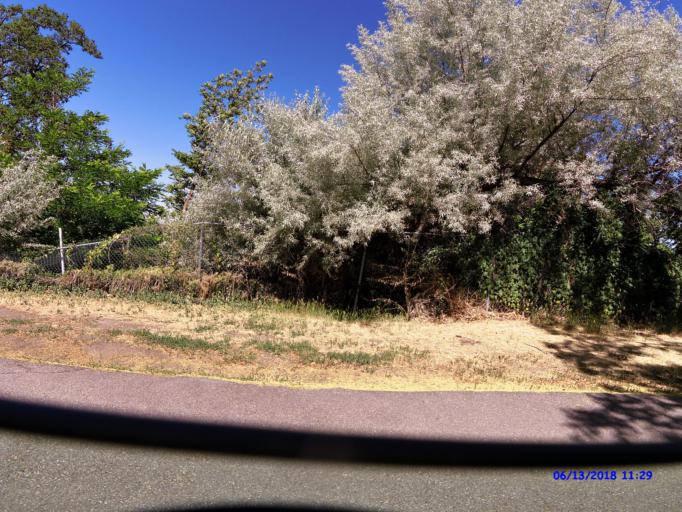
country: US
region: Utah
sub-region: Weber County
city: Ogden
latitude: 41.2343
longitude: -111.9645
